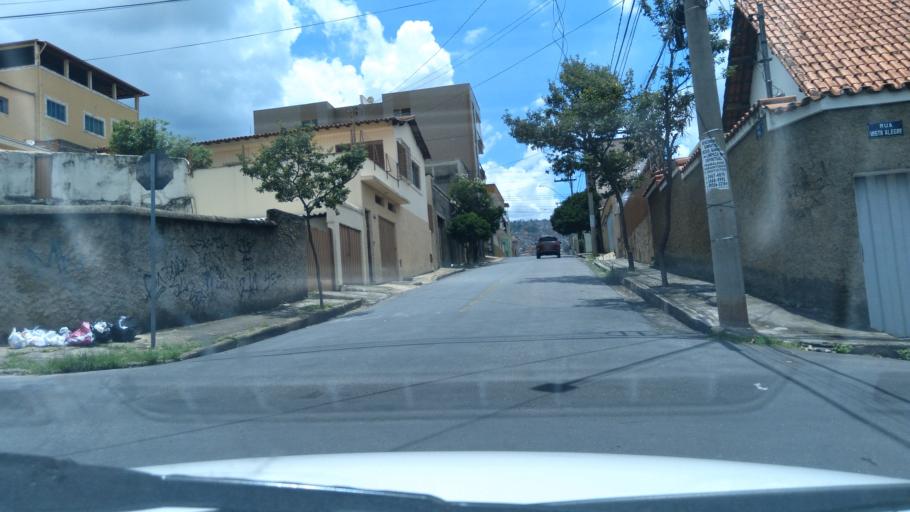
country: BR
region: Minas Gerais
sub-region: Belo Horizonte
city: Belo Horizonte
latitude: -19.9218
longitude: -43.9101
